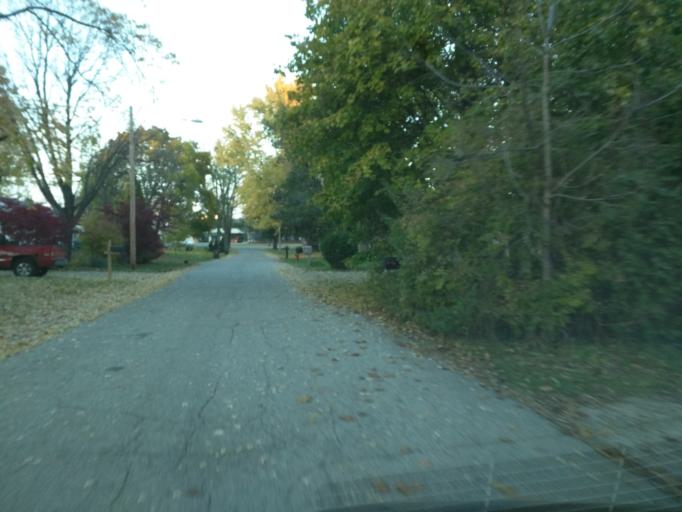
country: US
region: Michigan
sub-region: Ingham County
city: Edgemont Park
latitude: 42.7630
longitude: -84.5825
